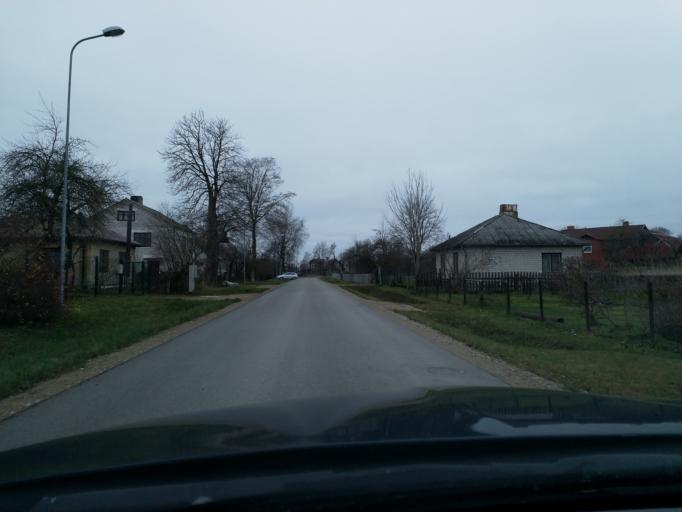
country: LV
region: Kuldigas Rajons
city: Kuldiga
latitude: 56.9707
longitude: 21.9946
